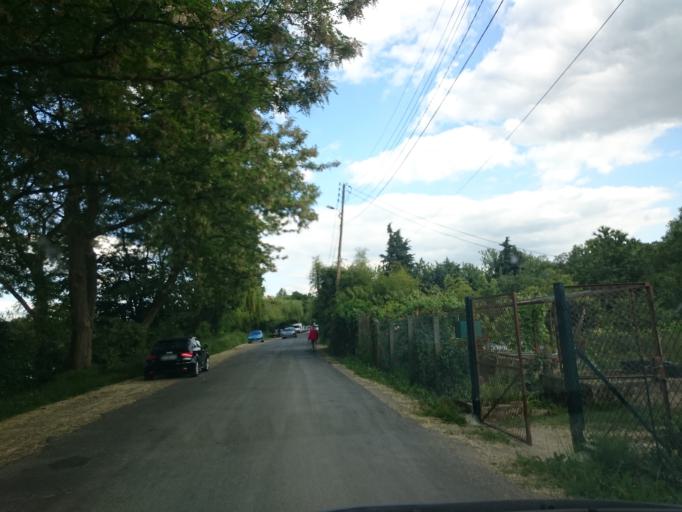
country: FR
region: Ile-de-France
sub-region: Departement de l'Essonne
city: Viry-Chatillon
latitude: 48.6644
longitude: 2.3852
